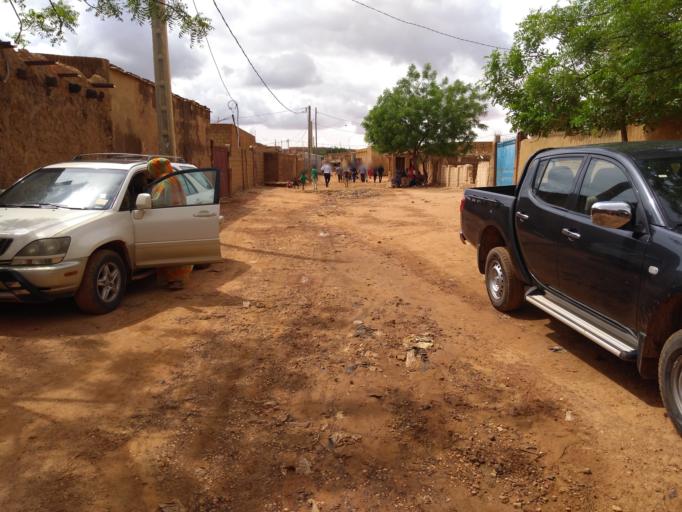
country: NE
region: Niamey
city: Niamey
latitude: 13.4817
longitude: 2.1509
